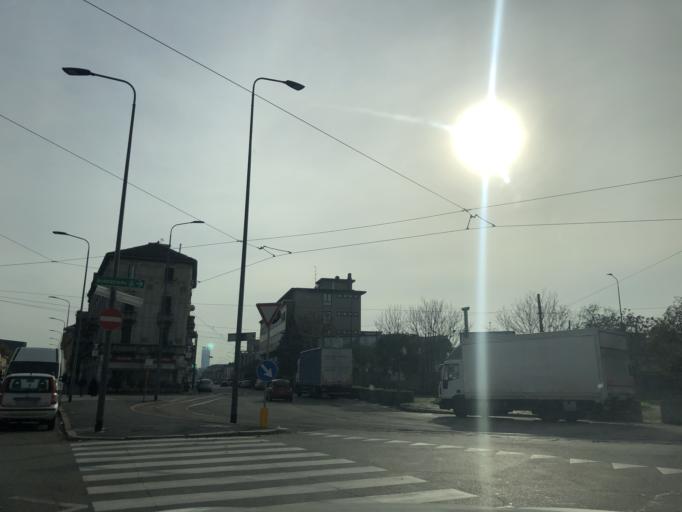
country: IT
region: Lombardy
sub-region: Citta metropolitana di Milano
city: Novate Milanese
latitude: 45.5051
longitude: 9.1368
